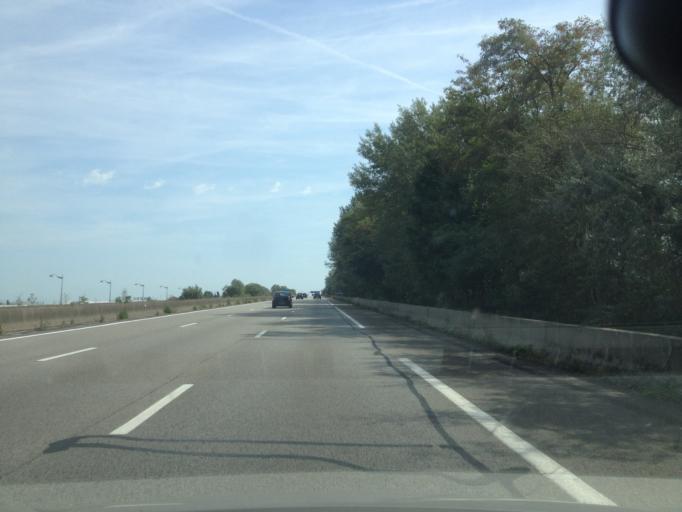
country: FR
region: Ile-de-France
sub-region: Departement des Yvelines
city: Buchelay
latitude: 48.9870
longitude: 1.6640
